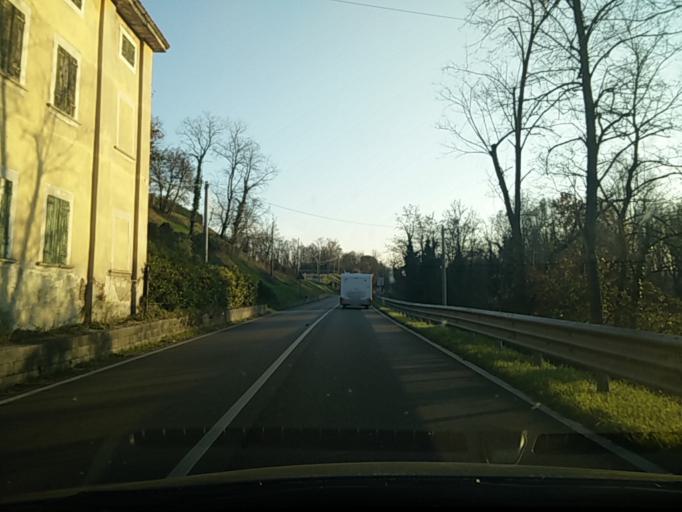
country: IT
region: Veneto
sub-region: Provincia di Verona
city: Salionze
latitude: 45.4139
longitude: 10.7179
